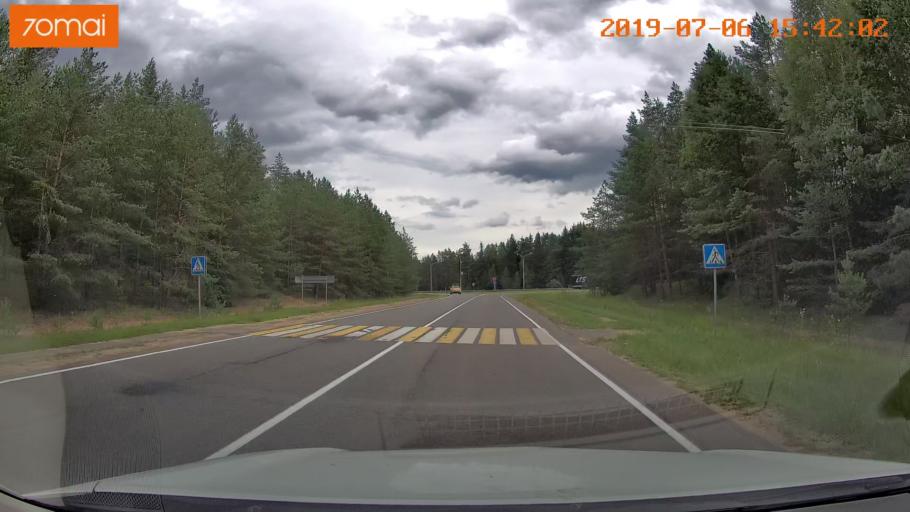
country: BY
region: Minsk
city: Rakaw
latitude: 53.9857
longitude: 26.9901
